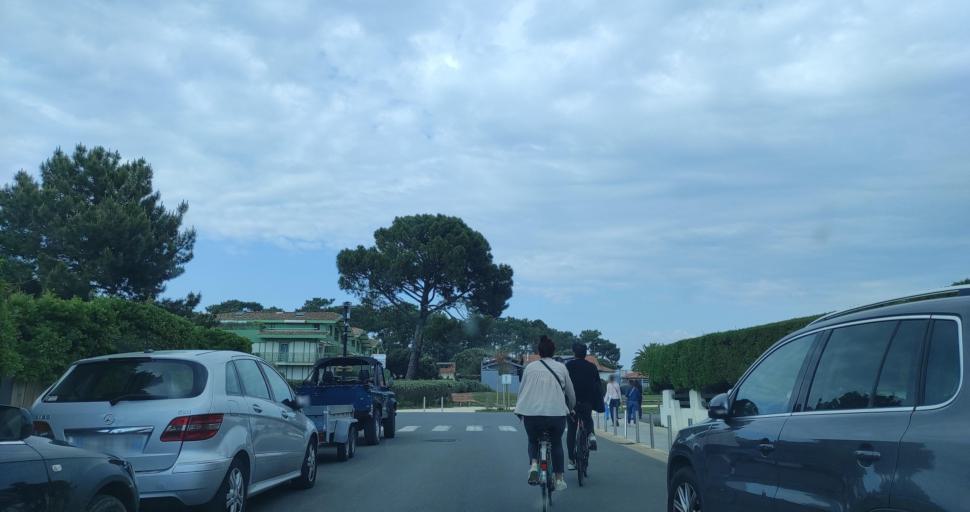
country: FR
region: Aquitaine
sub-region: Departement de la Gironde
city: Arcachon
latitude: 44.6552
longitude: -1.2406
